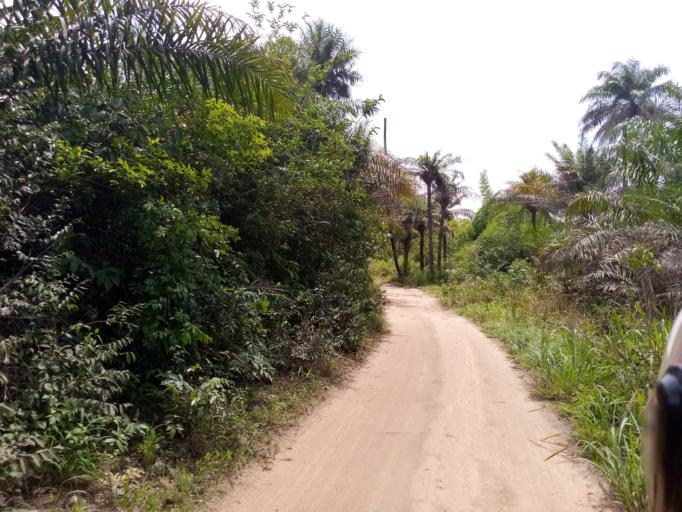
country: SL
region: Western Area
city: Waterloo
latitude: 8.3695
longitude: -13.0018
